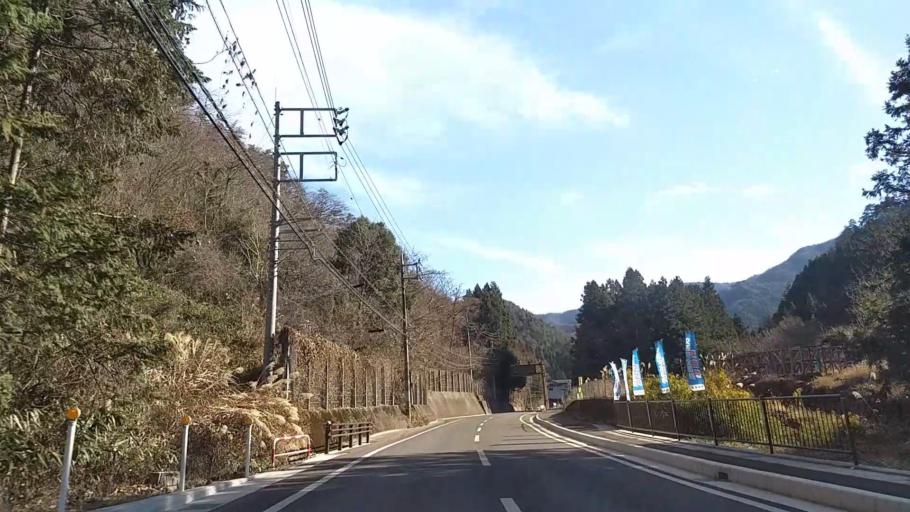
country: JP
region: Yamanashi
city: Otsuki
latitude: 35.5267
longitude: 138.9228
